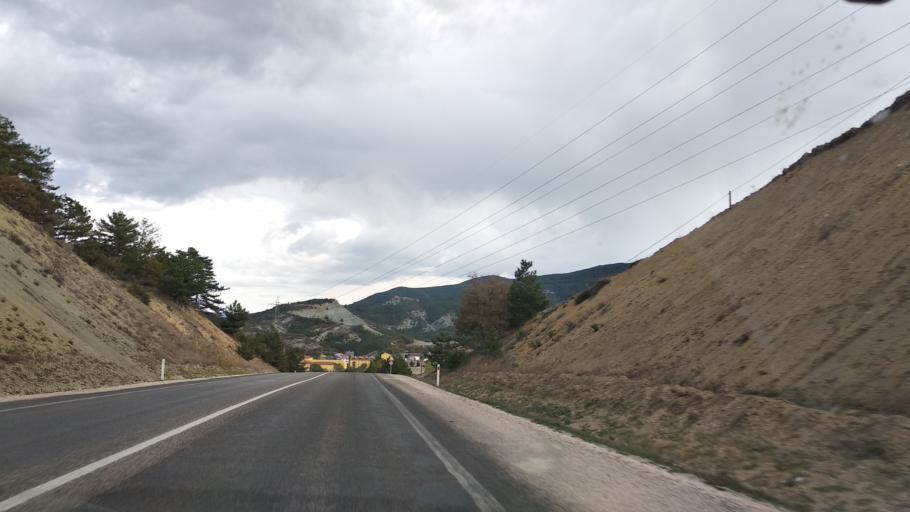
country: TR
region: Bolu
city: Mudurnu
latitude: 40.4861
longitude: 31.1923
